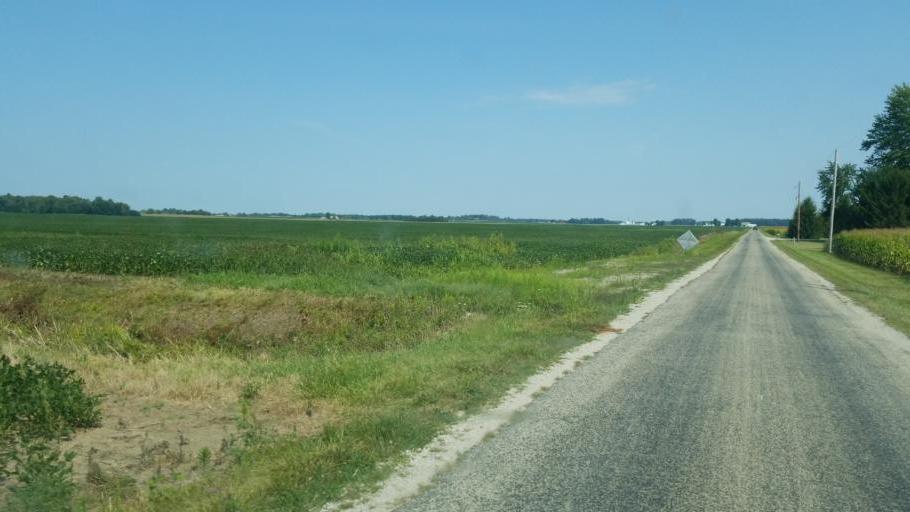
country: US
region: Ohio
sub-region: Crawford County
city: Bucyrus
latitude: 40.9362
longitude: -82.8731
